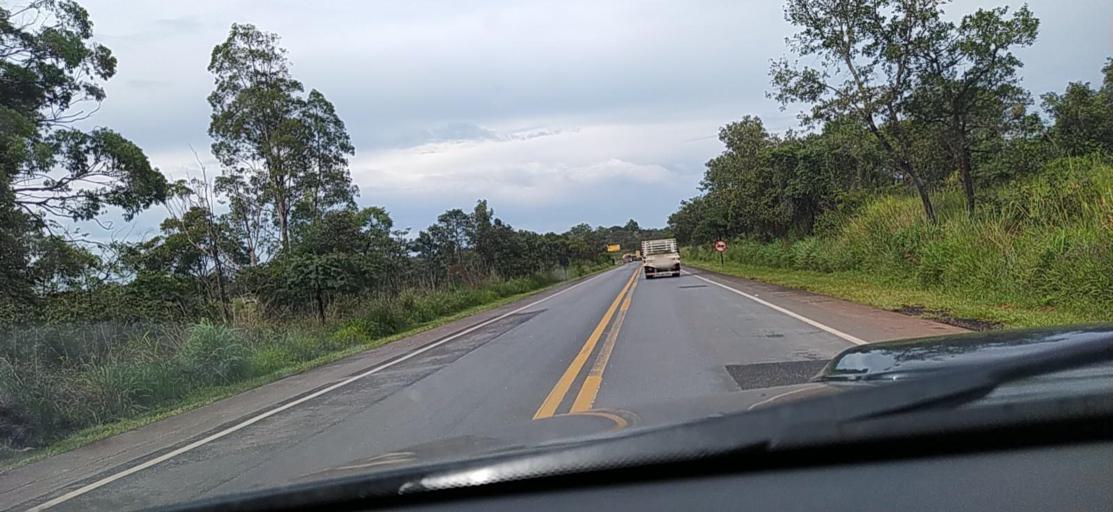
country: BR
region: Minas Gerais
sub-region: Montes Claros
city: Montes Claros
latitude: -16.8739
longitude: -43.8581
